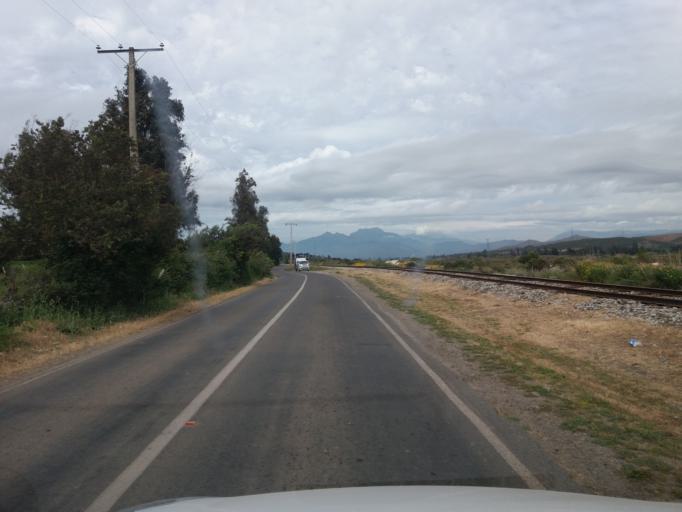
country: CL
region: Valparaiso
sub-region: Provincia de Marga Marga
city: Quilpue
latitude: -32.9163
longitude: -71.4191
